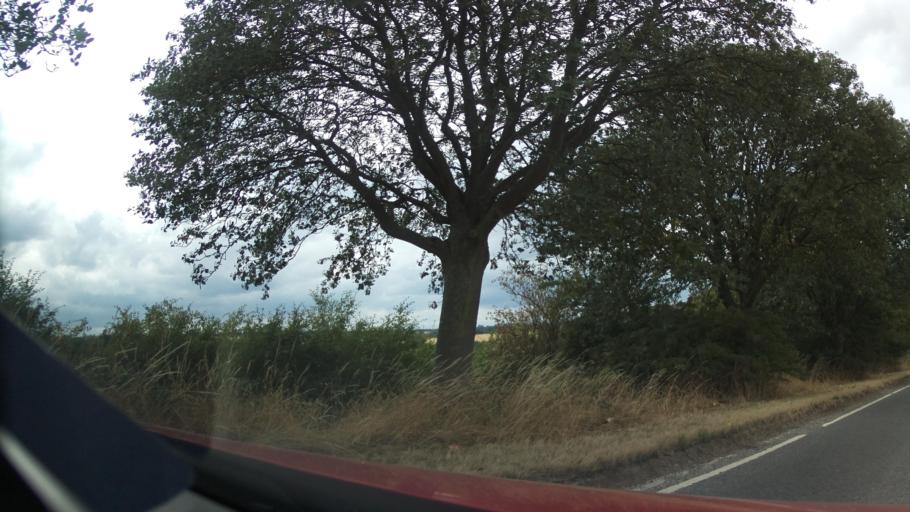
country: GB
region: England
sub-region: Leicestershire
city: Castle Donington
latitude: 52.8022
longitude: -1.3734
